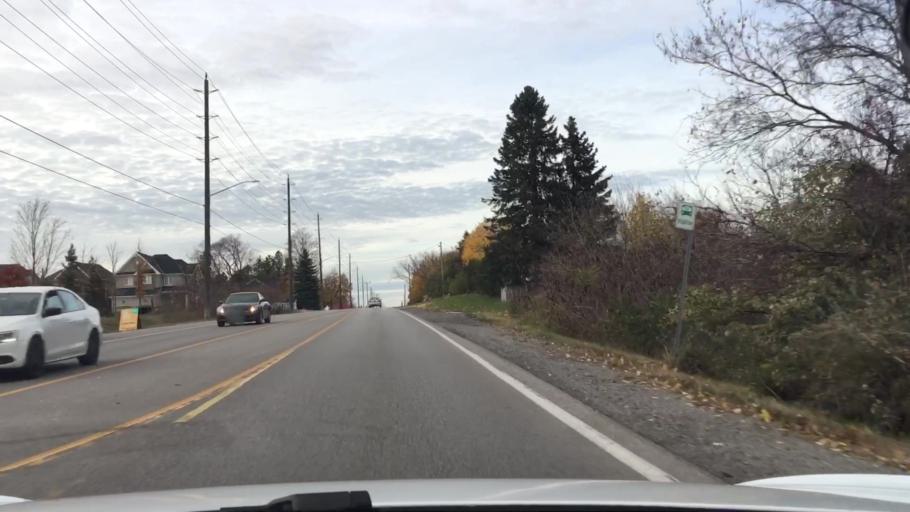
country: CA
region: Ontario
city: Oshawa
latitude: 43.9356
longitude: -78.8261
